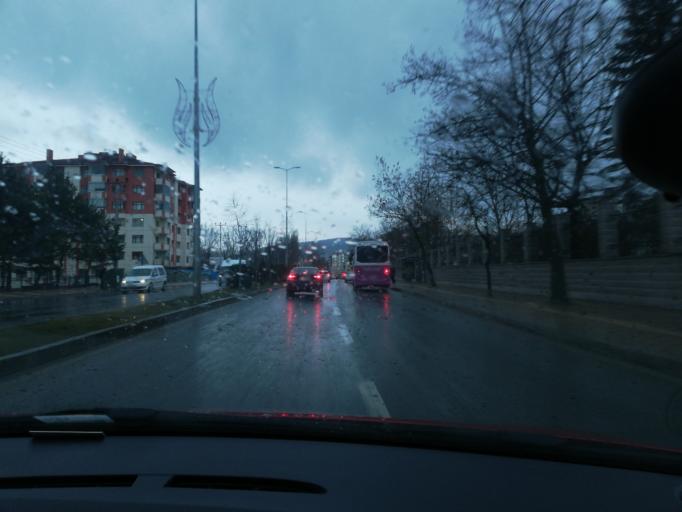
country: TR
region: Kastamonu
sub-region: Cide
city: Kastamonu
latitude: 41.4098
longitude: 33.7898
